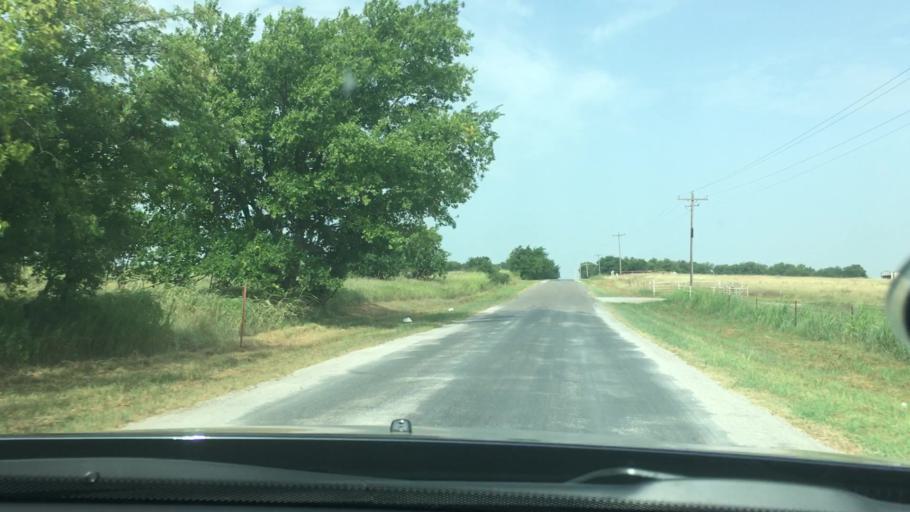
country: US
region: Oklahoma
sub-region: Garvin County
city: Pauls Valley
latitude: 34.7967
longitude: -97.1645
